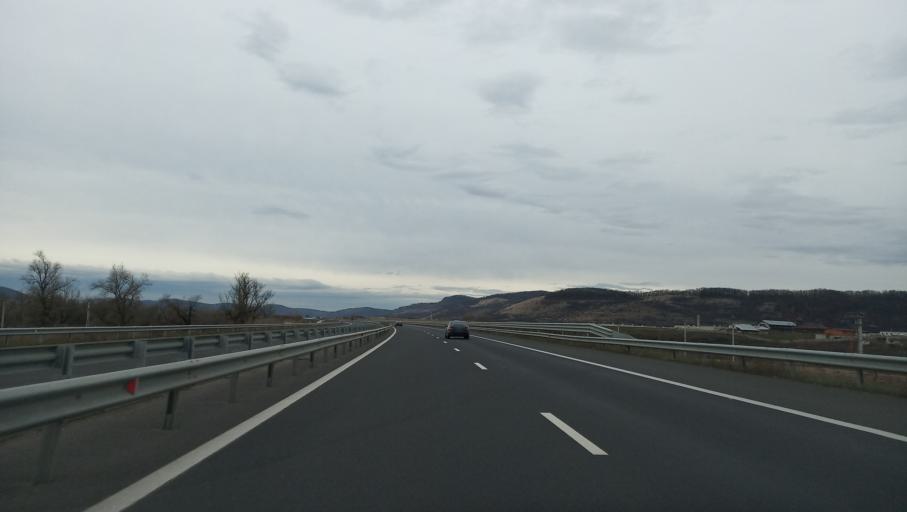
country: RO
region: Hunedoara
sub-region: Comuna Soimus
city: Soimus
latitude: 45.9069
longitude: 22.9214
